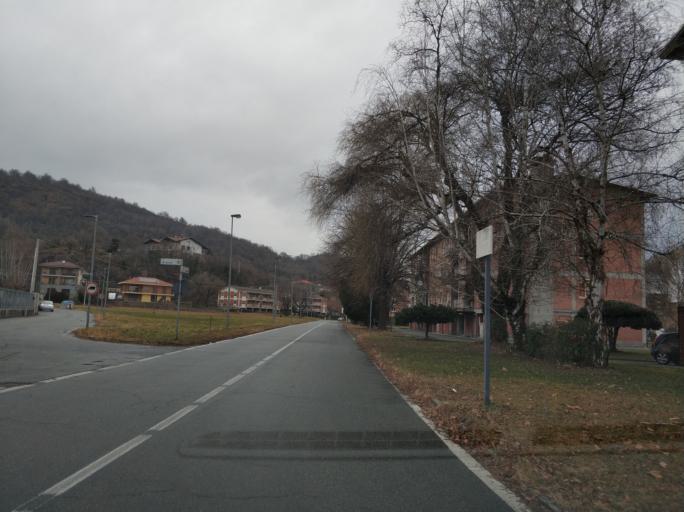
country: IT
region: Piedmont
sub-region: Provincia di Torino
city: Pavone Canavese
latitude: 45.4394
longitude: 7.8652
